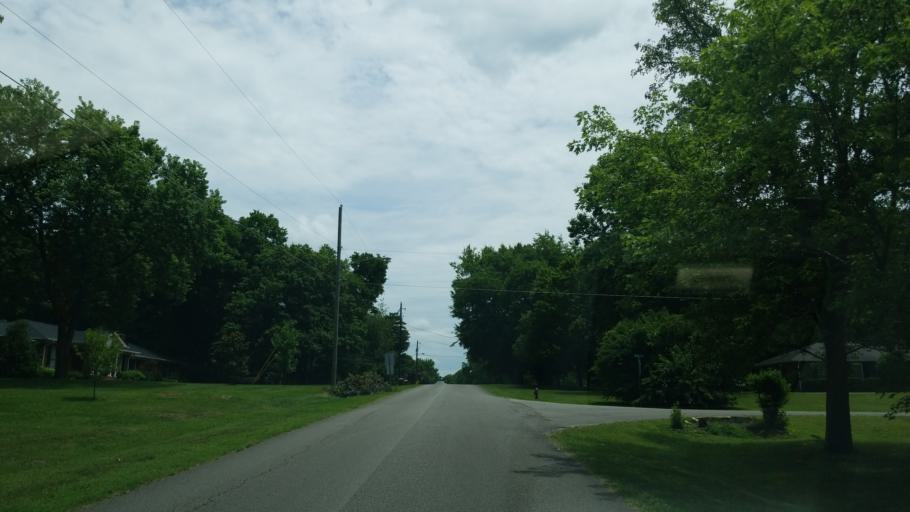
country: US
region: Tennessee
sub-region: Williamson County
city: Brentwood
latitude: 36.0302
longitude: -86.8062
